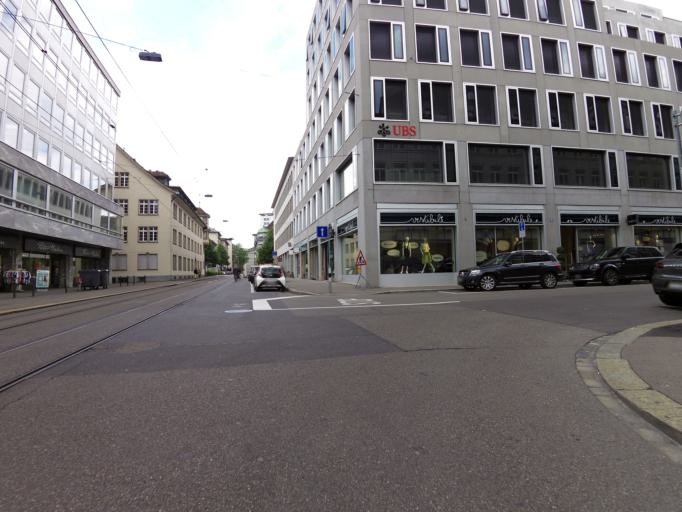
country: CH
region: Zurich
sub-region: Bezirk Zuerich
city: Zuerich (Kreis 1) / City
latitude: 47.3705
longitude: 8.5372
